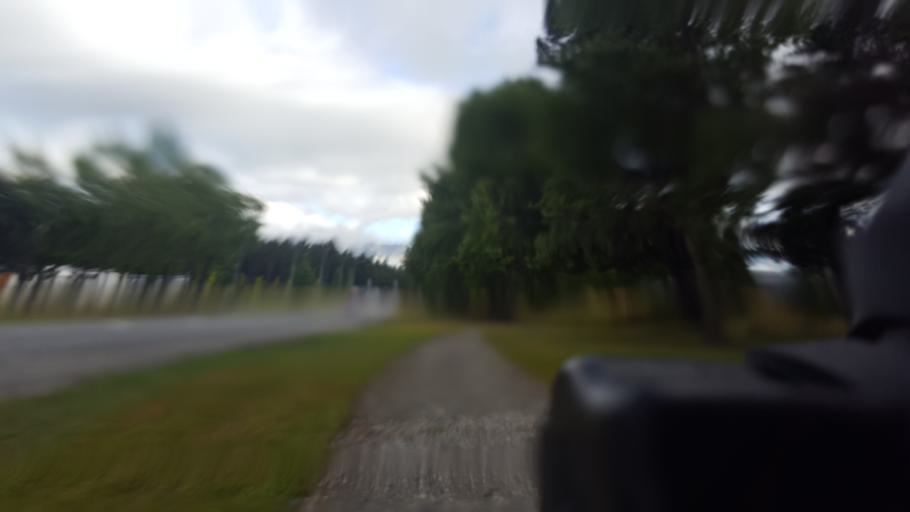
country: NZ
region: Otago
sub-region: Queenstown-Lakes District
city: Wanaka
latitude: -45.2430
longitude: 169.3781
